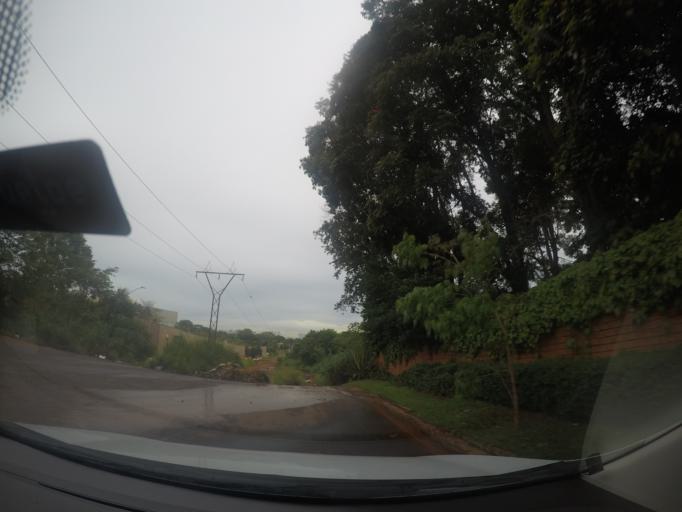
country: BR
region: Goias
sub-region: Goiania
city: Goiania
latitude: -16.6320
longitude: -49.2402
